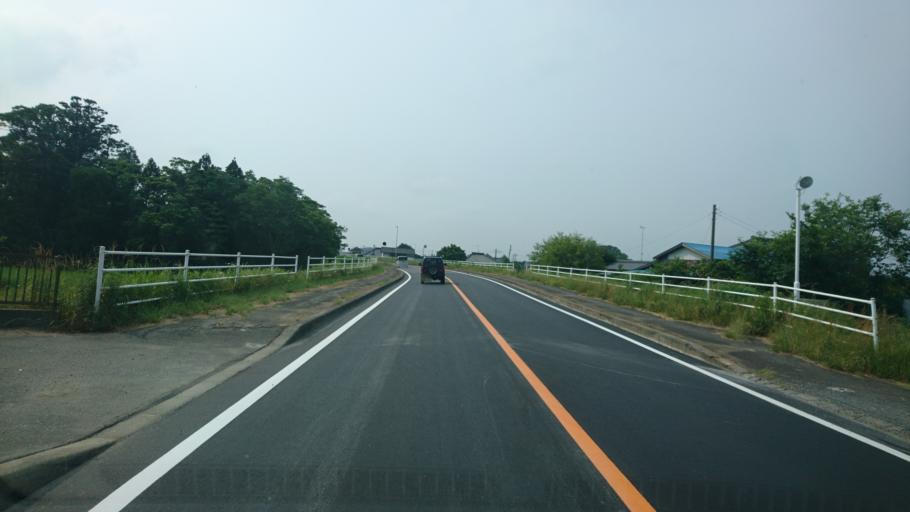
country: JP
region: Ibaraki
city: Edosaki
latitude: 35.8868
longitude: 140.3434
